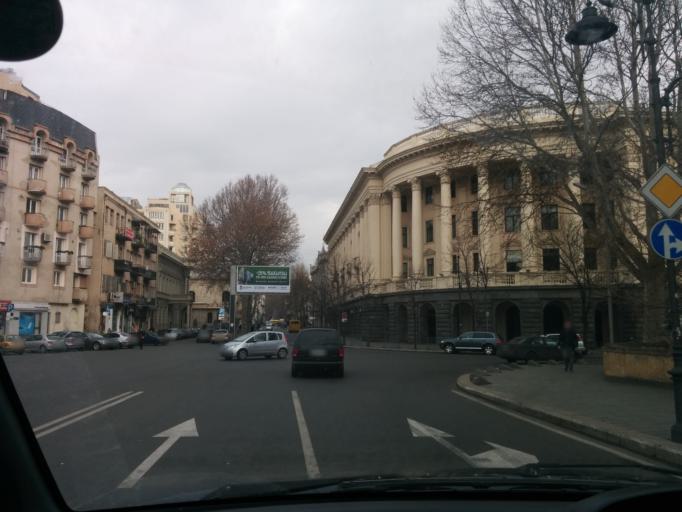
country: GE
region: T'bilisi
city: Tbilisi
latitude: 41.7079
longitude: 44.7932
